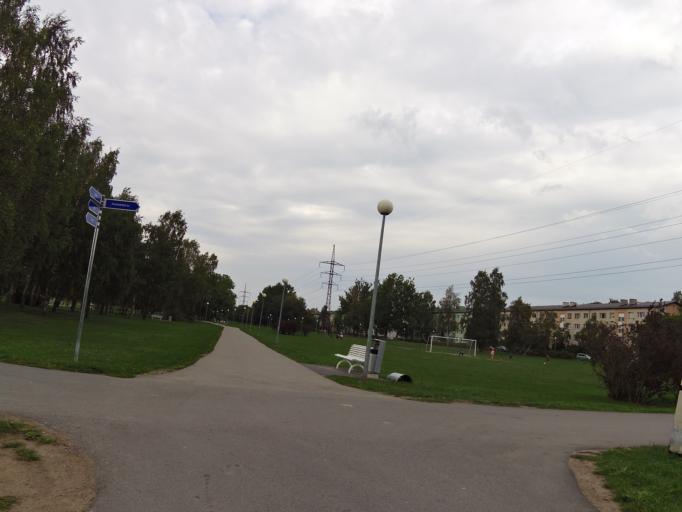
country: EE
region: Harju
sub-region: Tallinna linn
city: Tallinn
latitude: 59.4441
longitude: 24.6859
